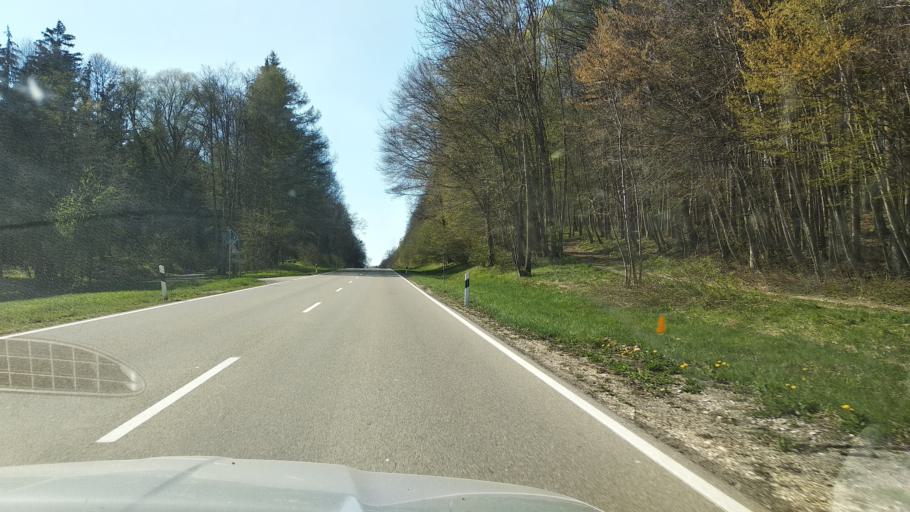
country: DE
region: Bavaria
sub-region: Swabia
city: Erkheim
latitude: 48.0453
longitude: 10.3909
